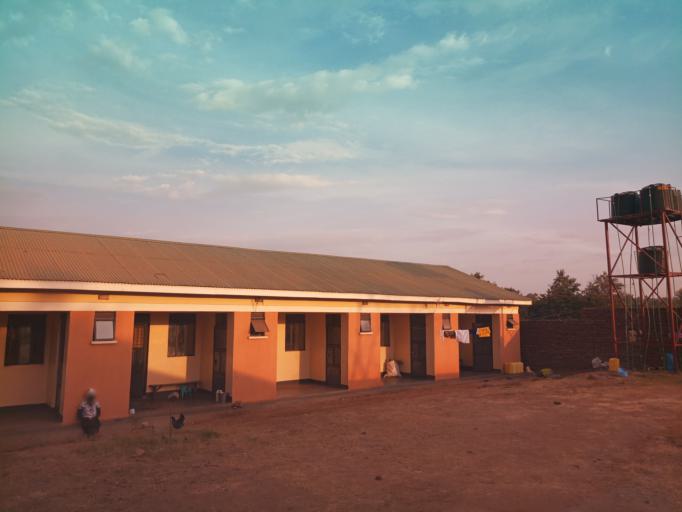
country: UG
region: Northern Region
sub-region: Arua District
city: Arua
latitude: 3.0341
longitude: 30.9209
